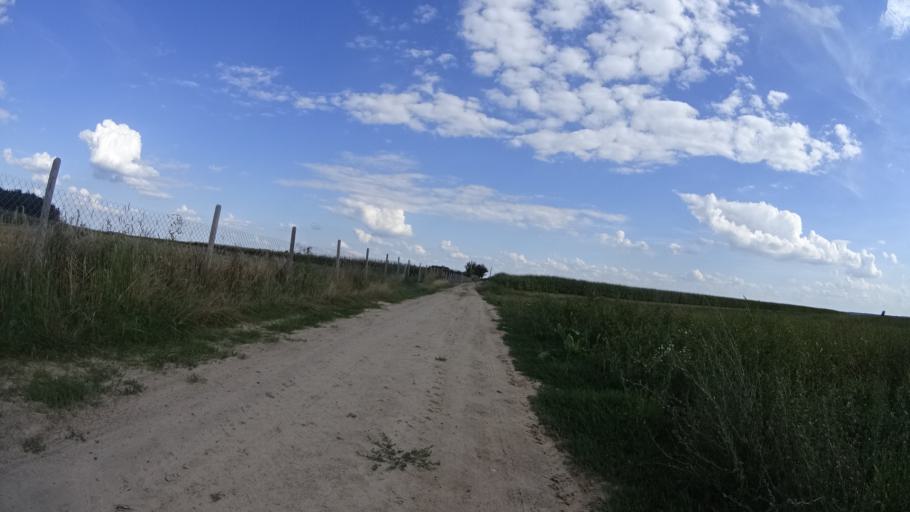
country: PL
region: Masovian Voivodeship
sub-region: Powiat bialobrzeski
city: Wysmierzyce
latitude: 51.6708
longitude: 20.8022
